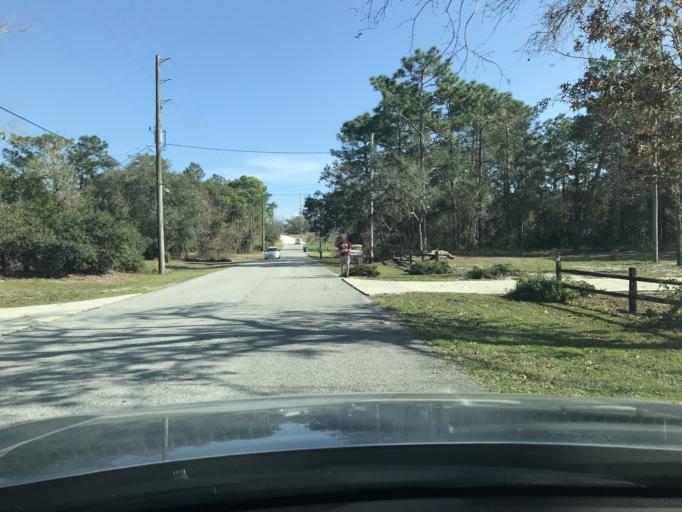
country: US
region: Florida
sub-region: Hernando County
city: North Weeki Wachee
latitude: 28.5427
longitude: -82.5452
